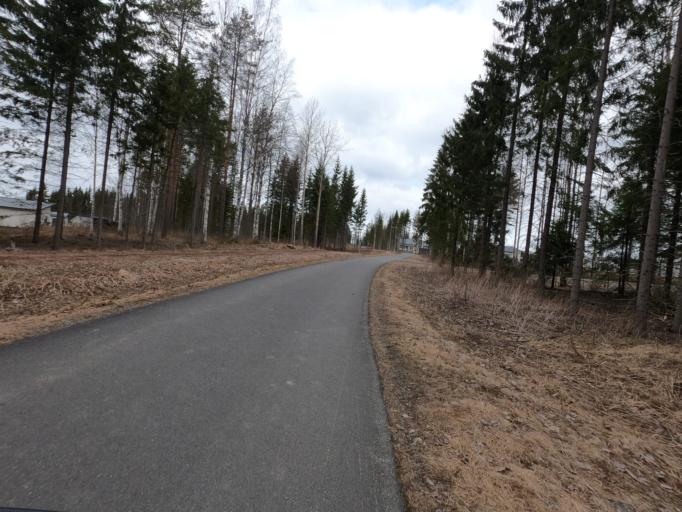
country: FI
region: North Karelia
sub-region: Joensuu
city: Joensuu
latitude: 62.5634
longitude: 29.8212
